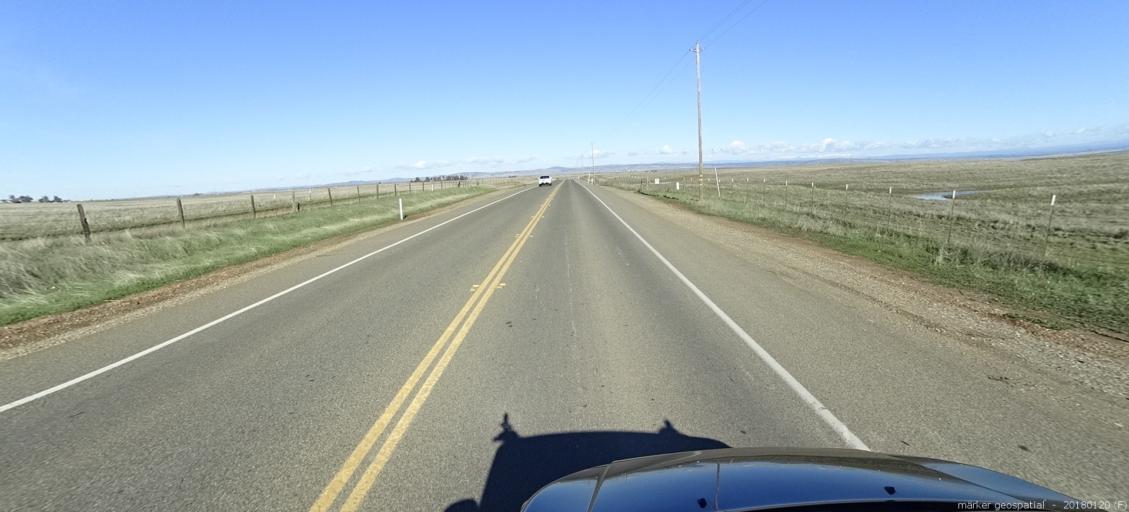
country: US
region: California
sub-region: Sacramento County
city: Rancho Murieta
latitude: 38.5296
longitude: -121.1923
